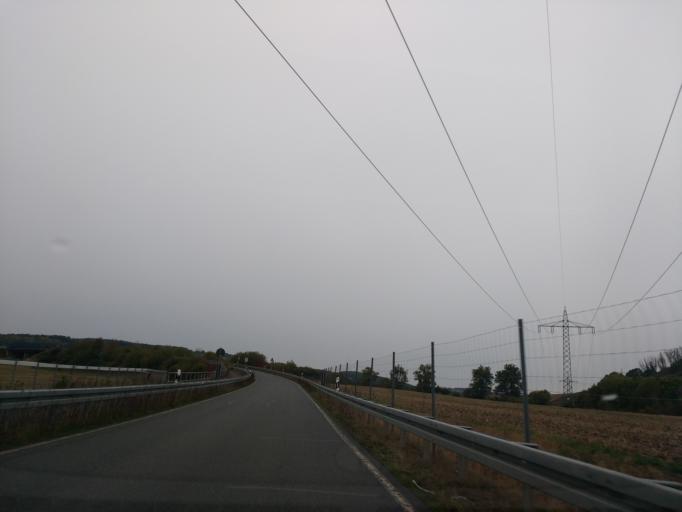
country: DE
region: Lower Saxony
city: Gemeinde Friedland
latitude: 51.4097
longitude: 9.9137
